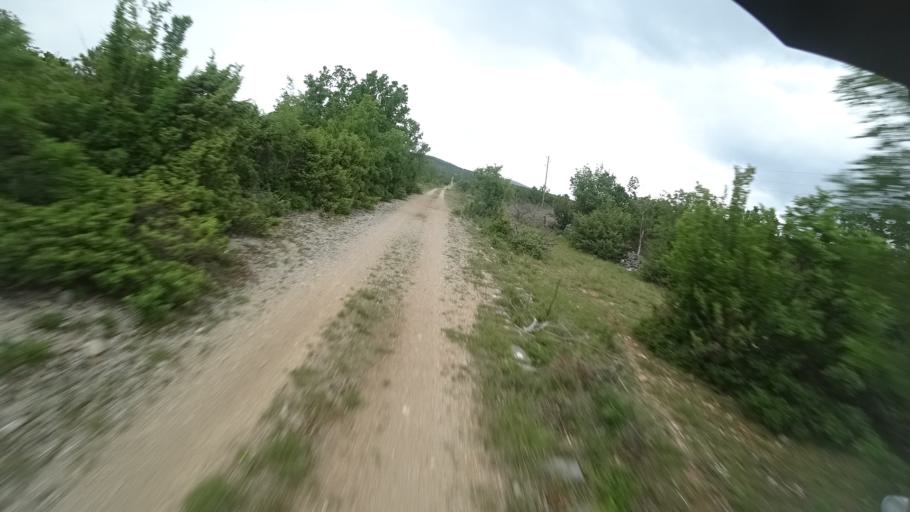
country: HR
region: Sibensko-Kniniska
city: Knin
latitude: 44.0223
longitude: 16.2628
